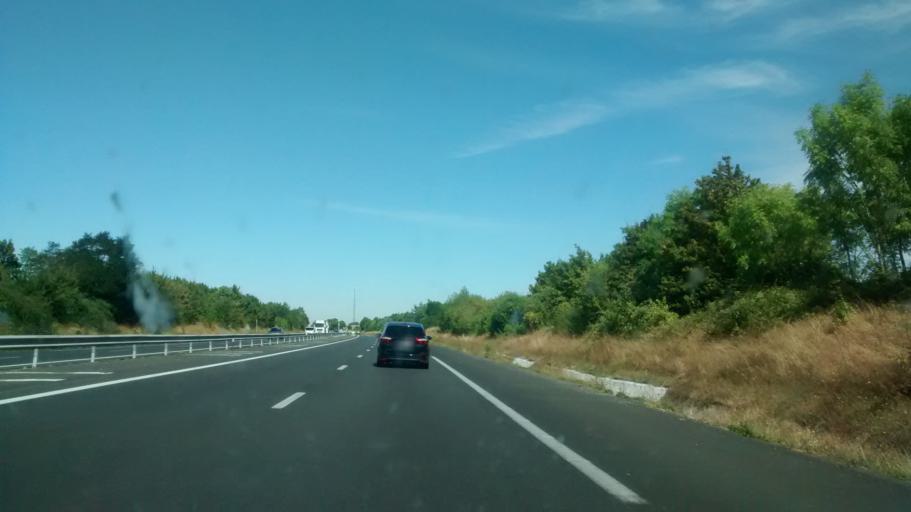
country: FR
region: Poitou-Charentes
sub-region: Departement de la Charente-Maritime
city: Saint-Jean-d'Angely
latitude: 46.0315
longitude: -0.5381
